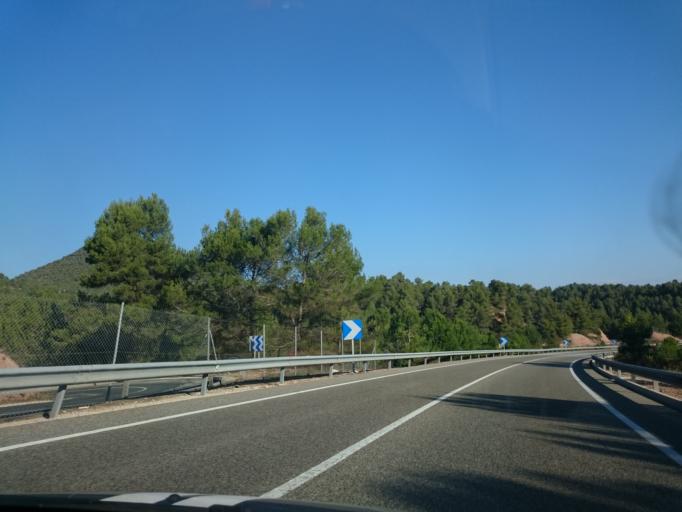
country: ES
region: Catalonia
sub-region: Provincia de Barcelona
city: Castellfollit del Boix
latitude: 41.6385
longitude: 1.6958
